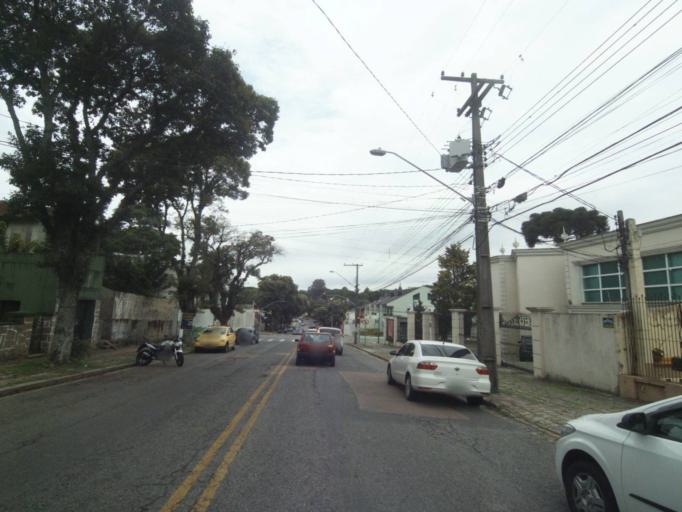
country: BR
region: Parana
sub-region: Curitiba
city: Curitiba
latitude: -25.4190
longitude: -49.2887
